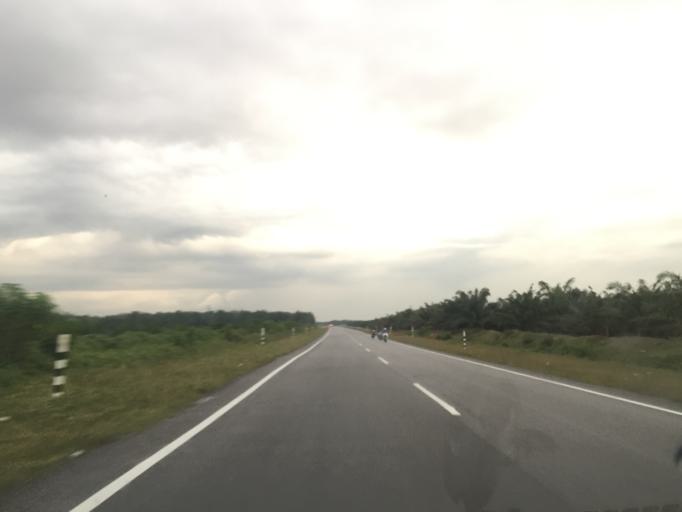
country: MY
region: Penang
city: Tasek Glugor
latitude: 5.5310
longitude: 100.5313
